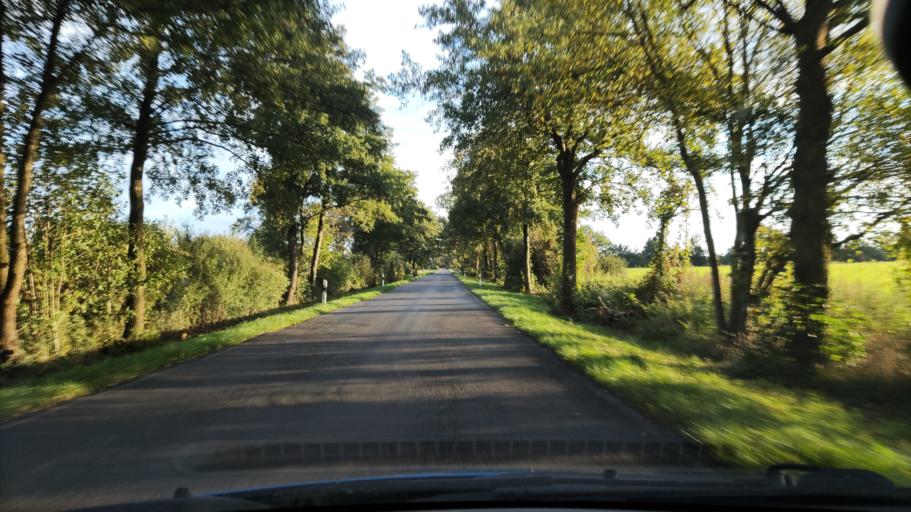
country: DE
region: Lower Saxony
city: Neu Darchau
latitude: 53.3639
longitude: 10.8645
